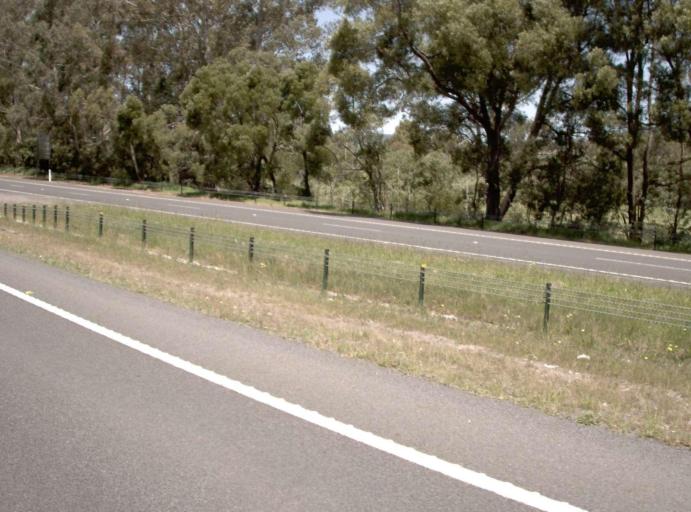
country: AU
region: Victoria
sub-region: Latrobe
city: Moe
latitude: -38.1839
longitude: 146.2759
